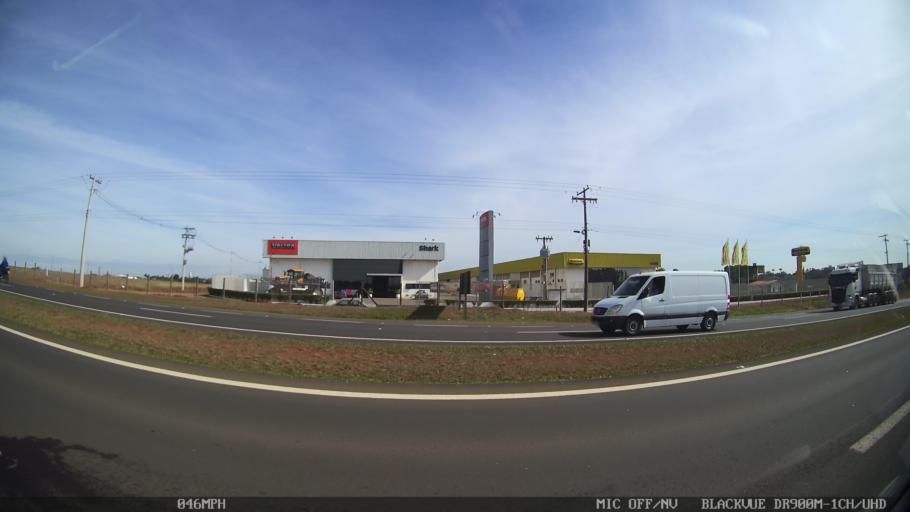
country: BR
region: Sao Paulo
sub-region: Piracicaba
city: Piracicaba
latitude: -22.7783
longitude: -47.6511
